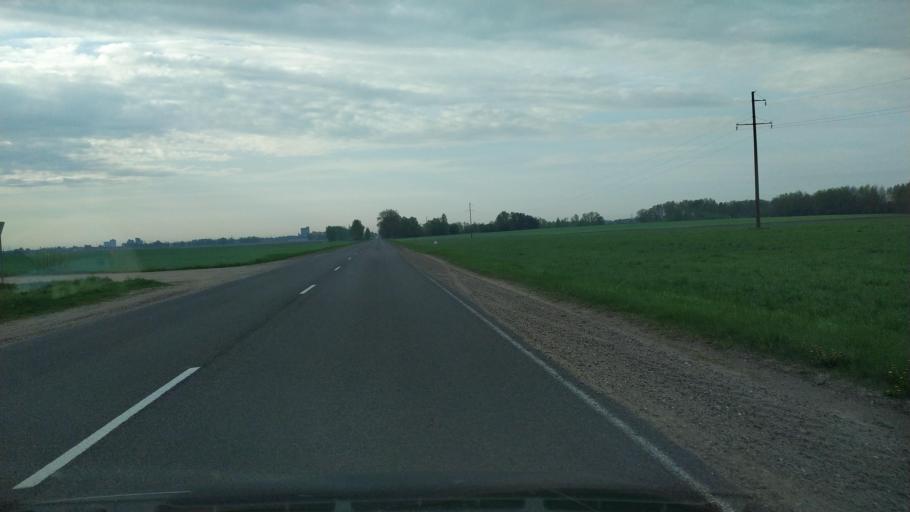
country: BY
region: Brest
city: Zhabinka
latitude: 52.2271
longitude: 23.9882
